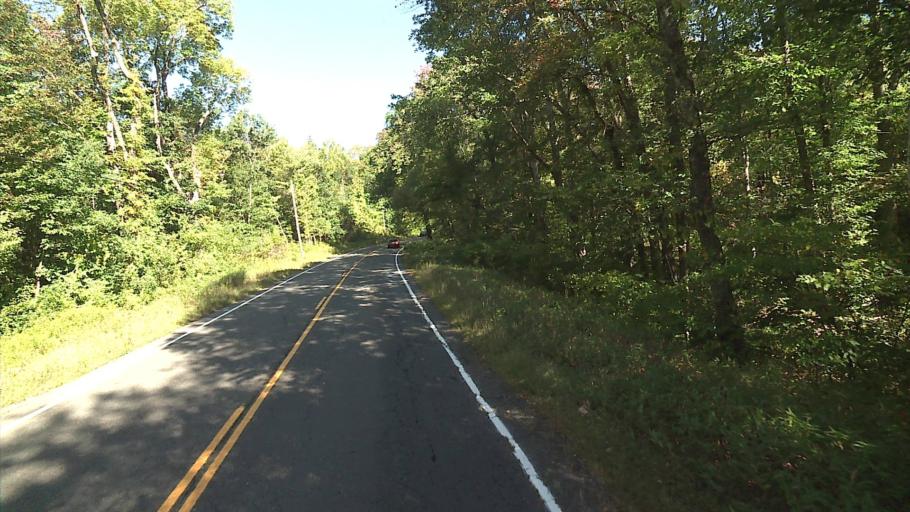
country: US
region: Connecticut
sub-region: Litchfield County
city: Terryville
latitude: 41.7533
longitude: -72.9771
